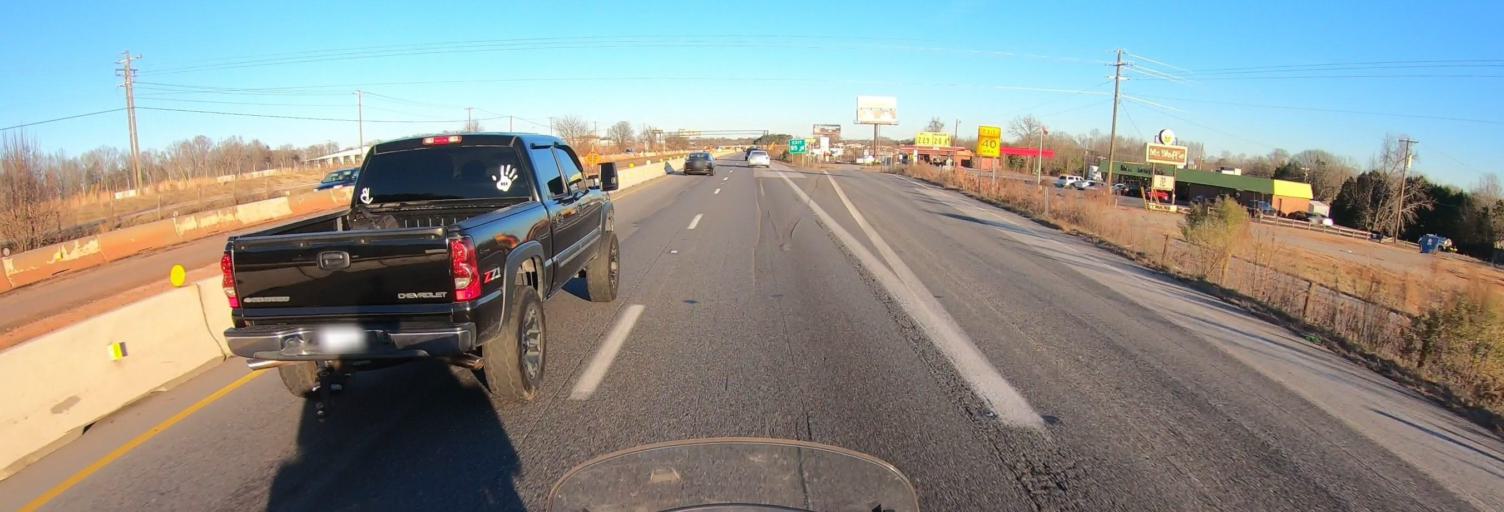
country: US
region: South Carolina
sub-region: Cherokee County
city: East Gaffney
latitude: 35.1014
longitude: -81.6362
